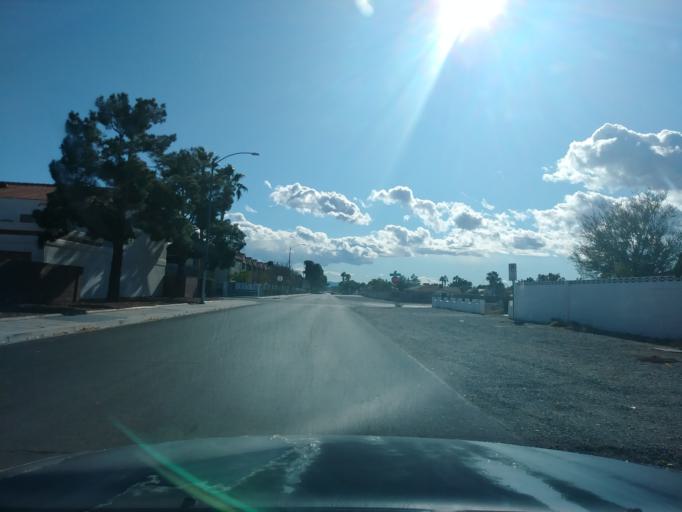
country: US
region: Nevada
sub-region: Clark County
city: Spring Valley
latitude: 36.1505
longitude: -115.2125
